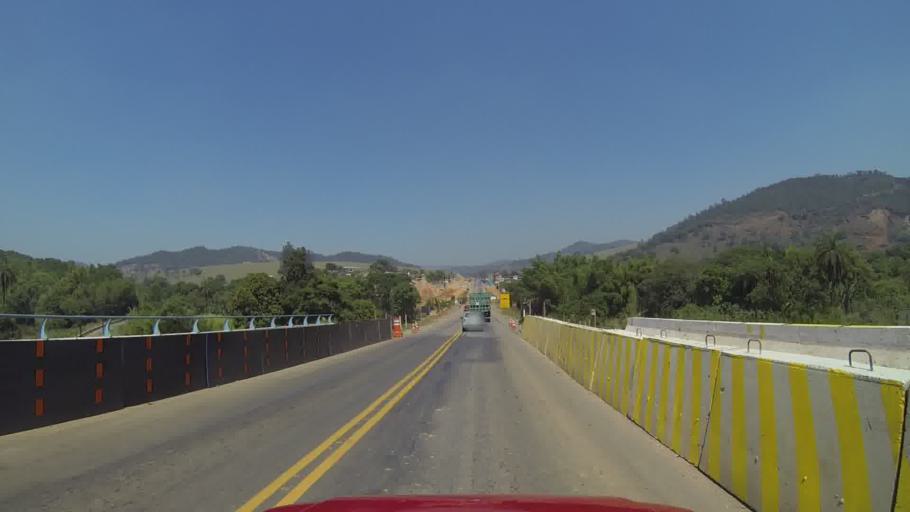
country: BR
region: Minas Gerais
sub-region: Mateus Leme
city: Mateus Leme
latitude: -20.0113
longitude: -44.4743
